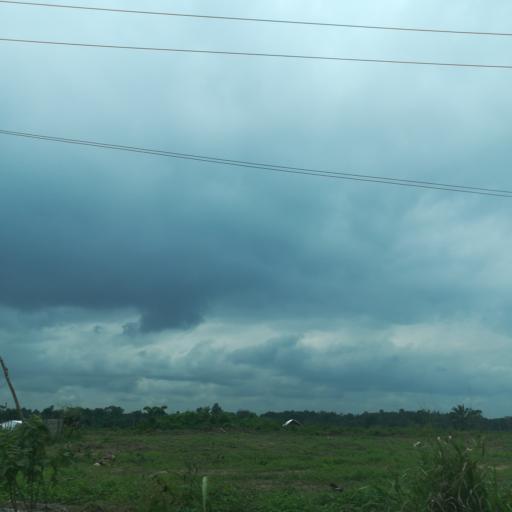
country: NG
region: Lagos
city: Ejirin
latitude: 6.6469
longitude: 3.8367
